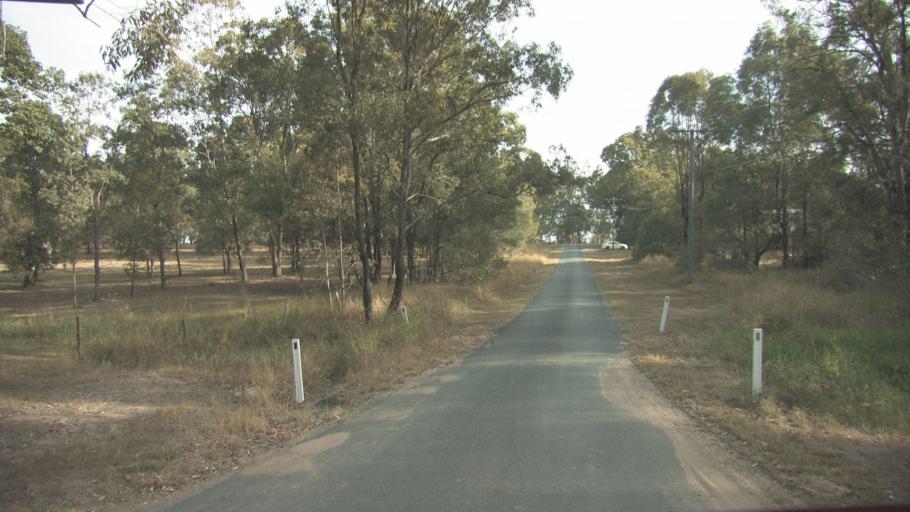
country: AU
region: Queensland
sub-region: Logan
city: Cedar Vale
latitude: -27.8718
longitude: 153.0247
